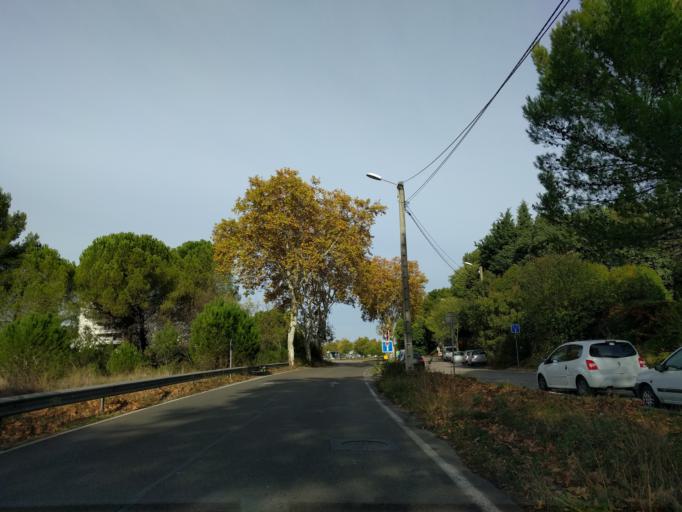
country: FR
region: Languedoc-Roussillon
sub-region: Departement de l'Herault
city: Montferrier-sur-Lez
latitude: 43.6368
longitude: 3.8483
